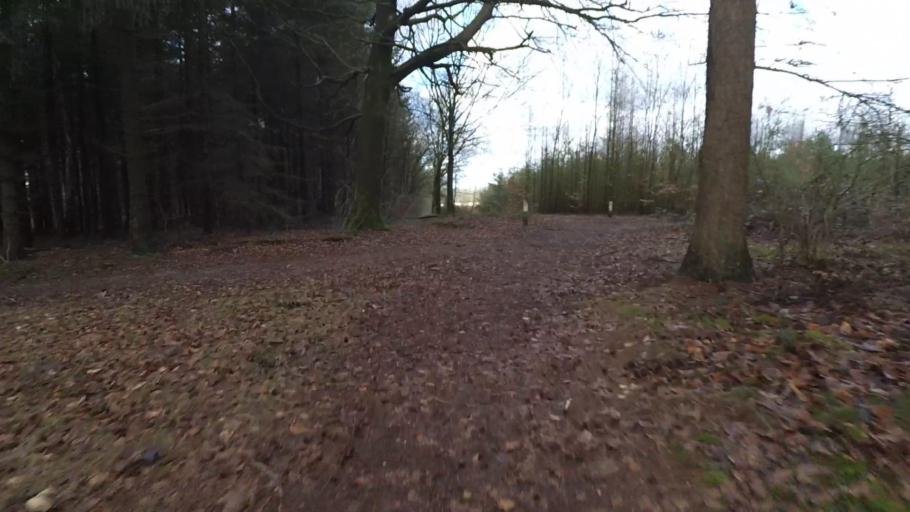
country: NL
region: Utrecht
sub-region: Gemeente Utrechtse Heuvelrug
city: Doorn
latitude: 52.0550
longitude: 5.3378
